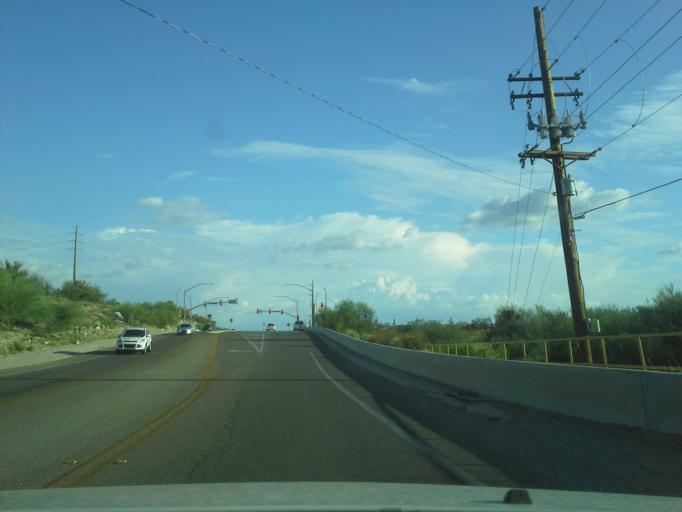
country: US
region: Arizona
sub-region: Pima County
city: Catalina Foothills
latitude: 32.3106
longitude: -110.8751
